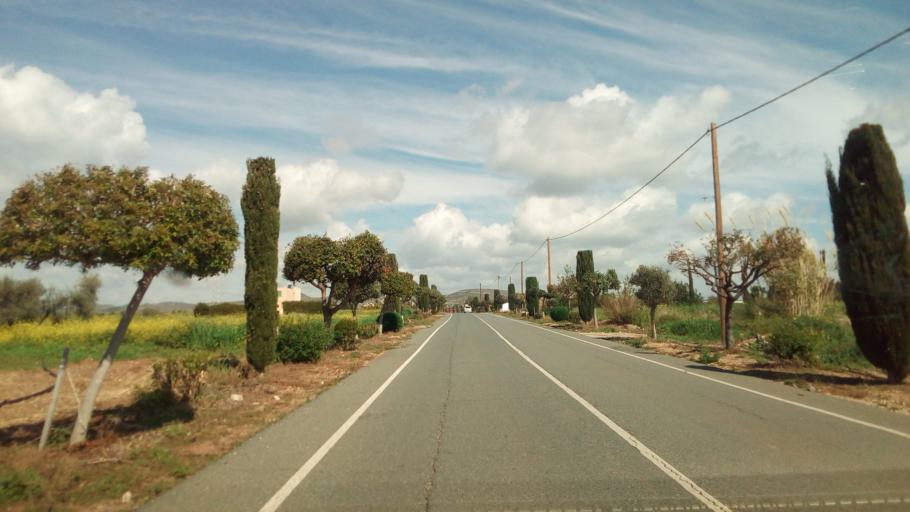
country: CY
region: Pafos
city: Mesogi
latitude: 34.7301
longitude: 32.5315
